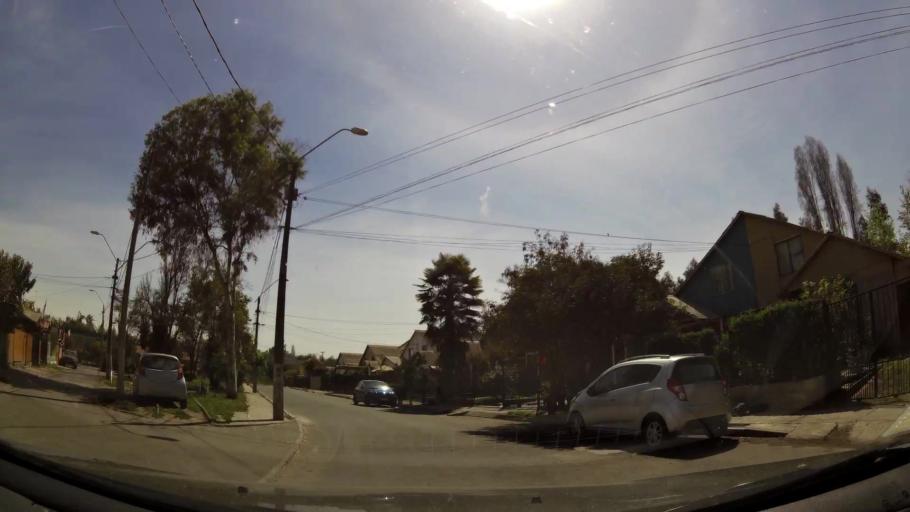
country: CL
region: Santiago Metropolitan
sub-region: Provincia de Cordillera
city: Puente Alto
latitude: -33.6285
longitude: -70.5754
